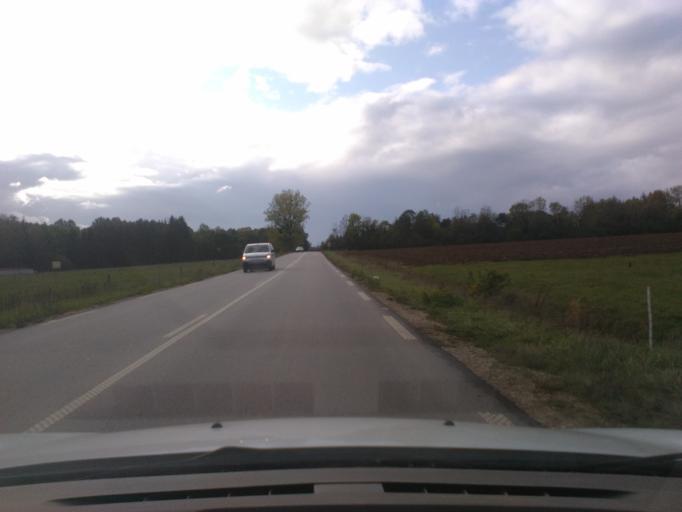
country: FR
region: Lorraine
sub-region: Departement des Vosges
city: Aydoilles
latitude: 48.2478
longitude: 6.6125
